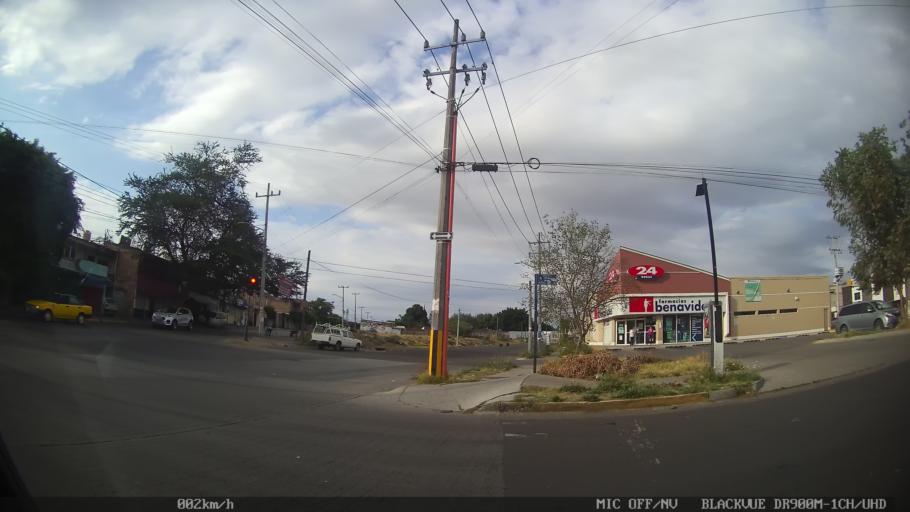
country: MX
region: Jalisco
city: Tlaquepaque
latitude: 20.6787
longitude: -103.2745
